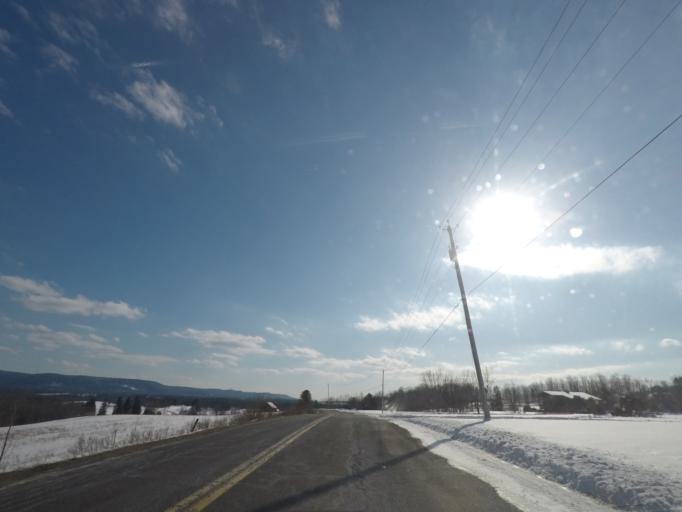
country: US
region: New York
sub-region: Rensselaer County
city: Hoosick Falls
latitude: 42.8587
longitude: -73.4986
